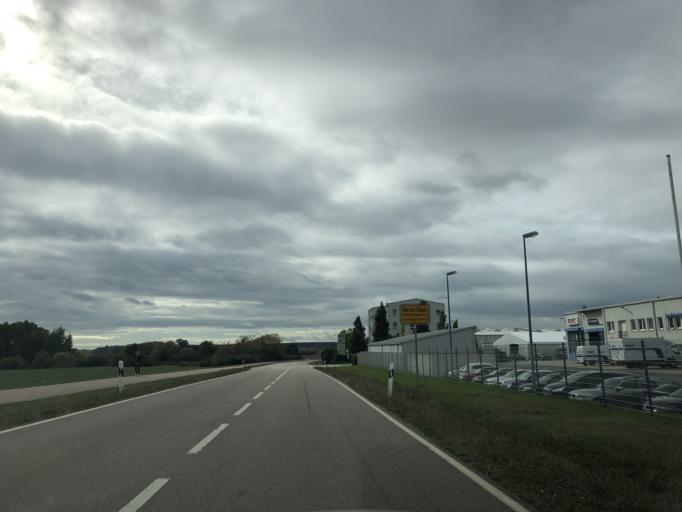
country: DE
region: Bavaria
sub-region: Regierungsbezirk Mittelfranken
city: Herzogenaurach
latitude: 49.5769
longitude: 10.9213
